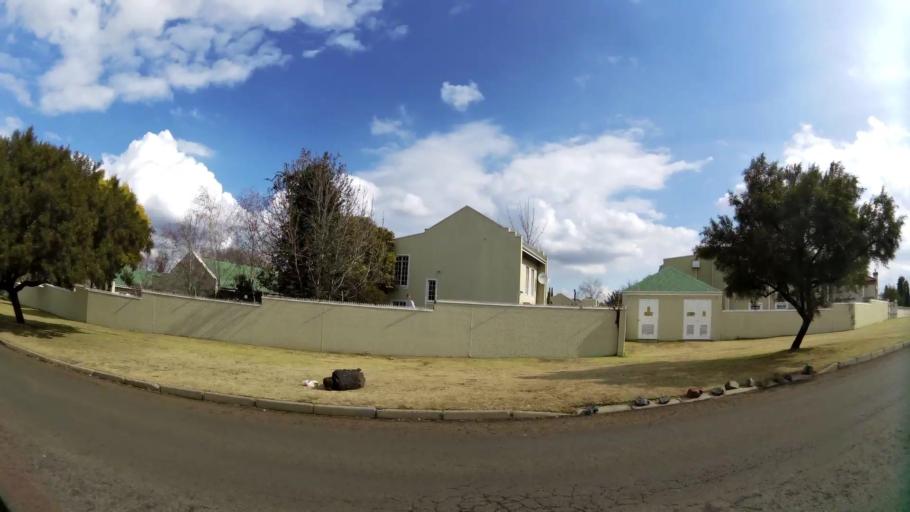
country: ZA
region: Gauteng
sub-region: Sedibeng District Municipality
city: Vanderbijlpark
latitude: -26.7470
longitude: 27.8296
